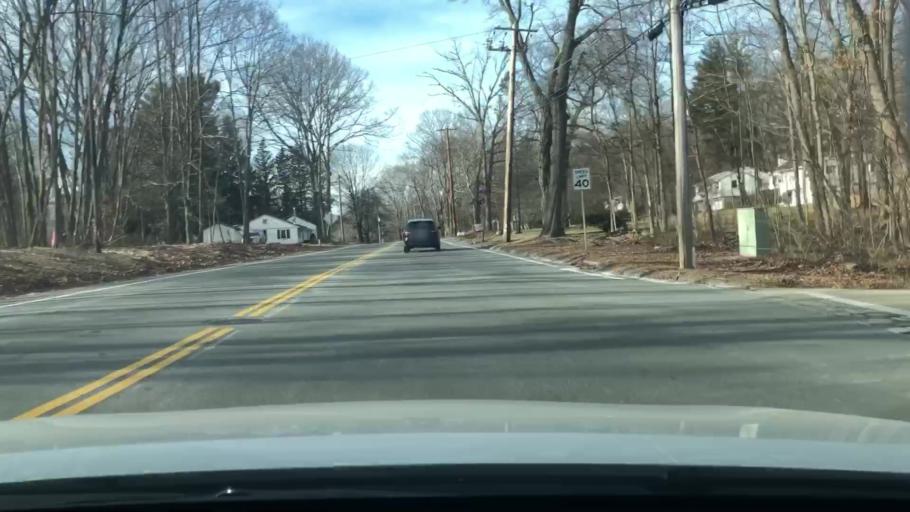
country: US
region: Massachusetts
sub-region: Worcester County
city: Grafton
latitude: 42.2051
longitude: -71.6734
